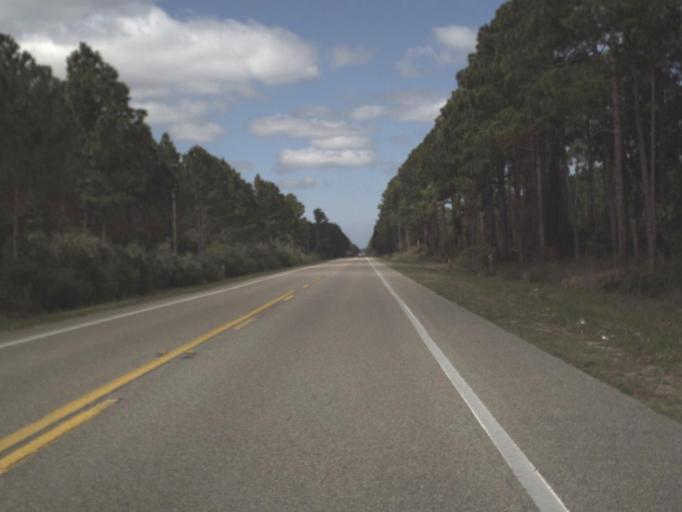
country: US
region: Florida
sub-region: Franklin County
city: Apalachicola
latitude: 29.7214
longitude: -85.1114
